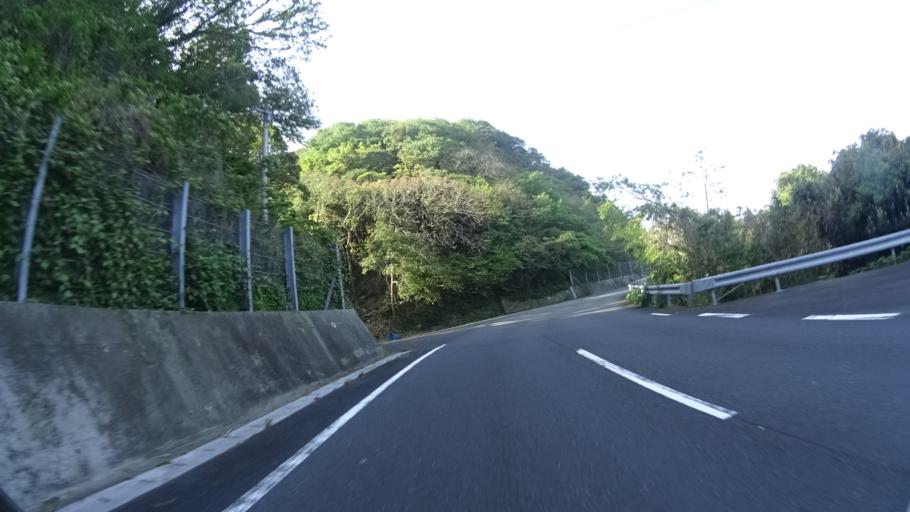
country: JP
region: Oita
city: Tsukumiura
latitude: 33.3645
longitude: 132.0398
